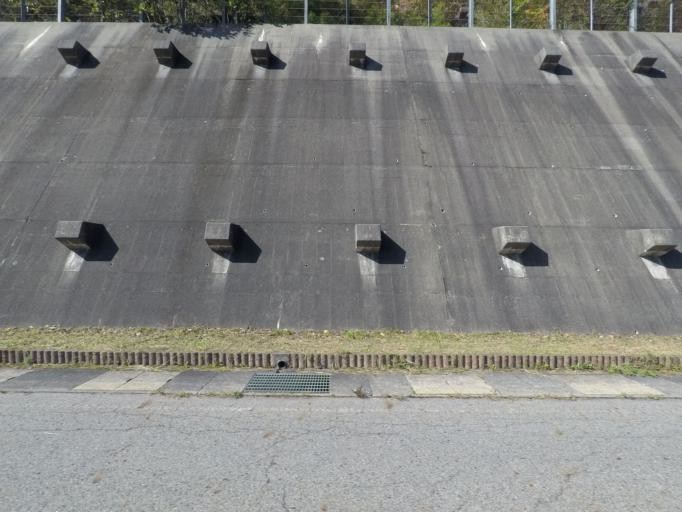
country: JP
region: Nagano
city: Tatsuno
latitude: 35.9754
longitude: 137.7677
